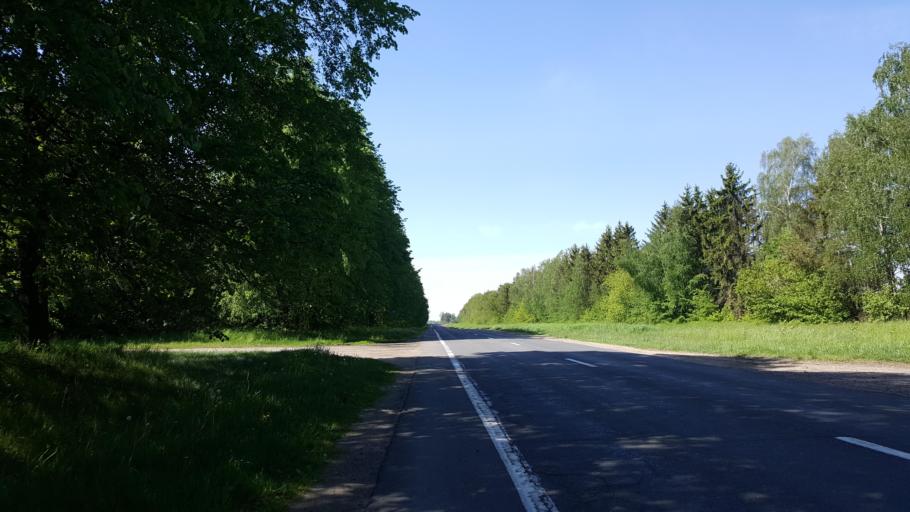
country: BY
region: Brest
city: Kamyanyets
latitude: 52.3763
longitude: 23.8015
